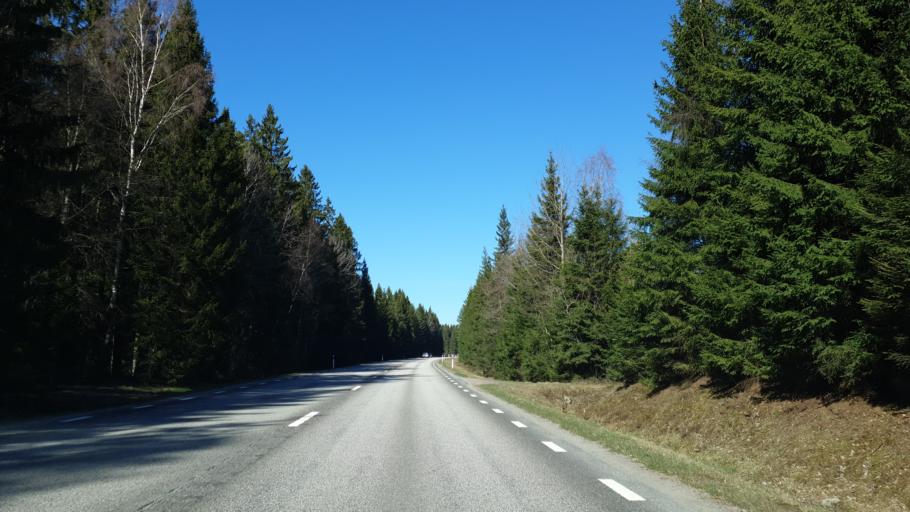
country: SE
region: Vaestra Goetaland
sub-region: Svenljunga Kommun
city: Svenljunga
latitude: 57.4747
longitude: 13.1110
